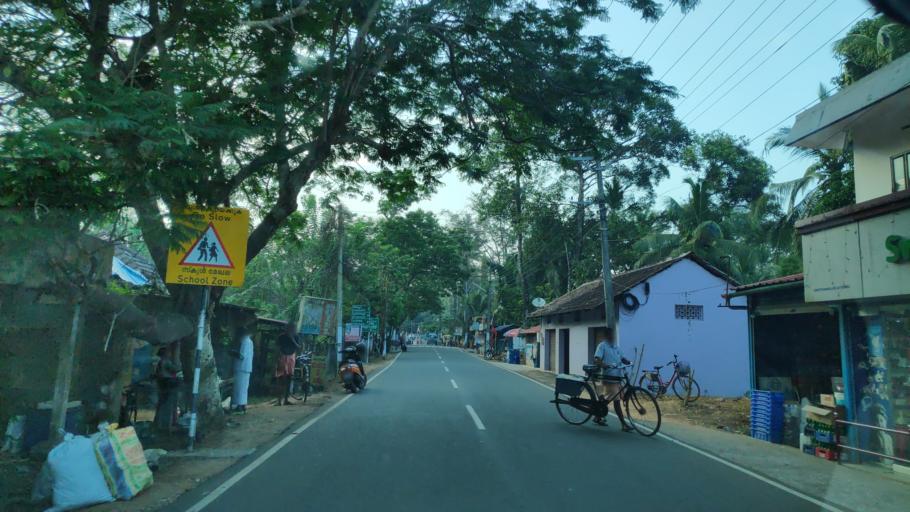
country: IN
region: Kerala
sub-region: Alappuzha
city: Shertallai
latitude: 9.6795
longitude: 76.3745
